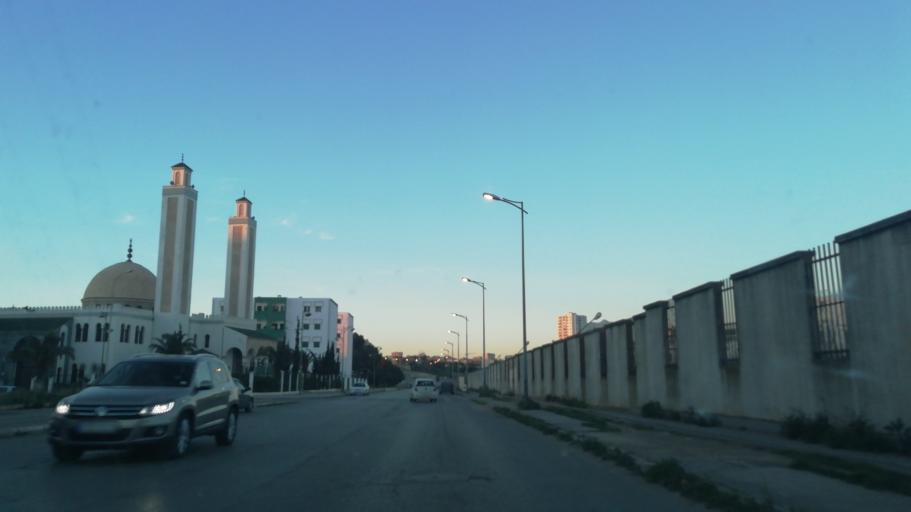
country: DZ
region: Oran
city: Bir el Djir
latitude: 35.7041
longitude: -0.5853
